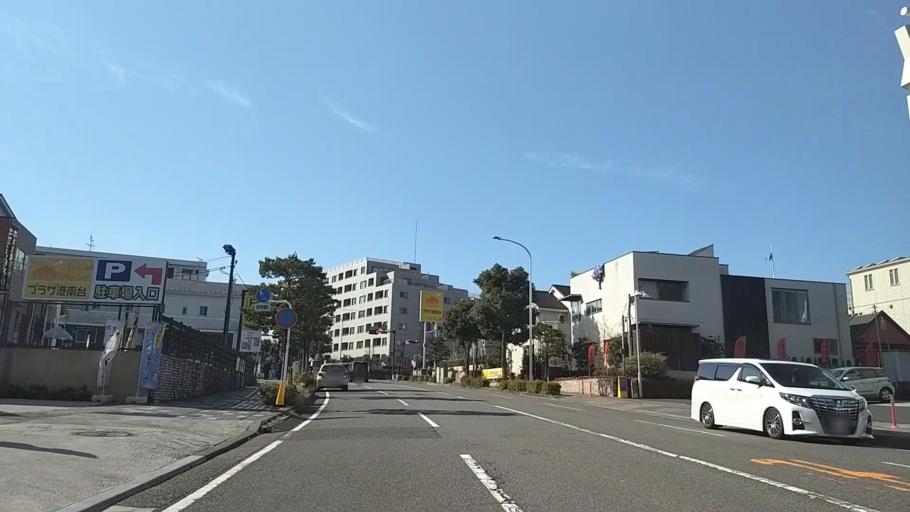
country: JP
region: Kanagawa
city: Kamakura
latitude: 35.3782
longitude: 139.5761
